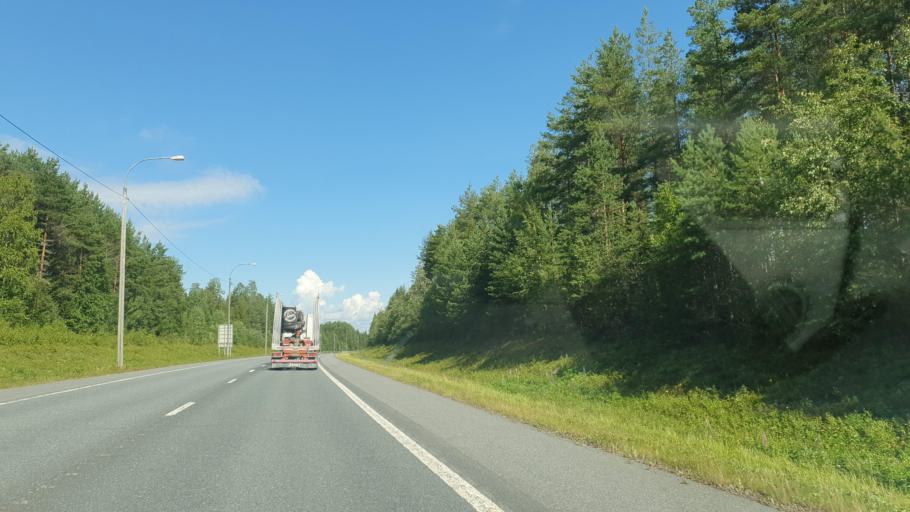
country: FI
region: Northern Savo
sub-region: Ylae-Savo
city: Iisalmi
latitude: 63.6027
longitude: 27.2154
